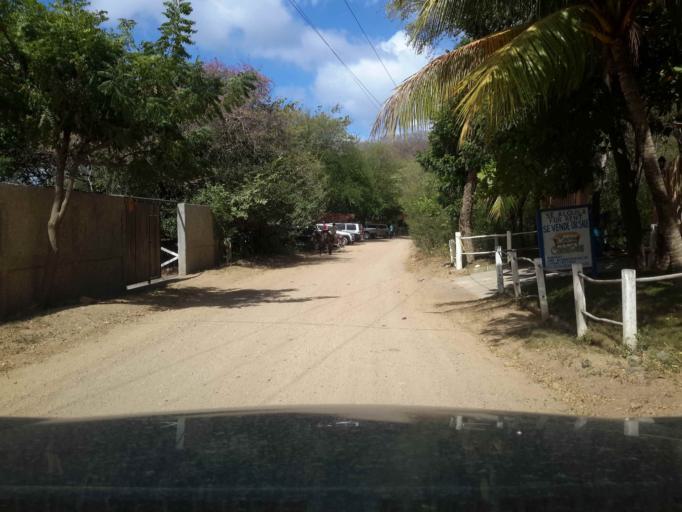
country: NI
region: Rivas
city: San Juan del Sur
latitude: 11.1583
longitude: -85.8017
